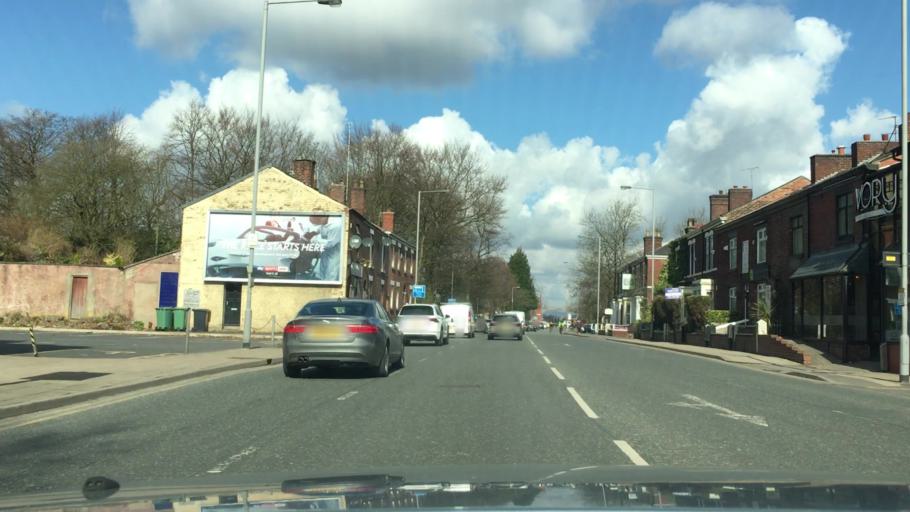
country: GB
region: England
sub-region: Borough of Bury
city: Whitefield
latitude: 53.5484
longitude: -2.2941
